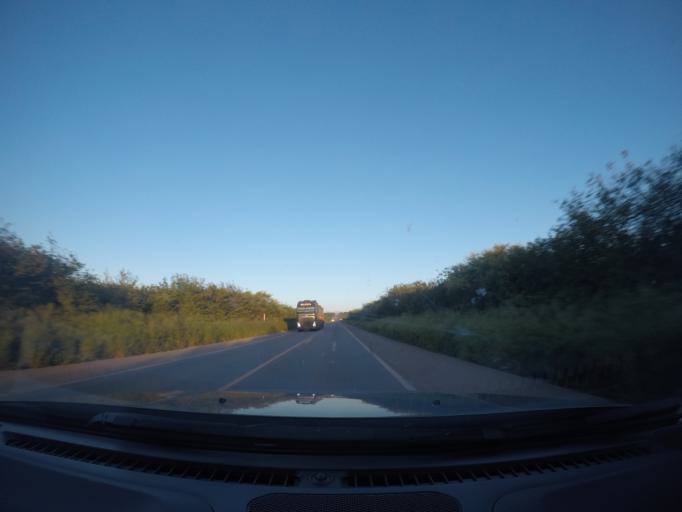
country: BR
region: Bahia
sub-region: Seabra
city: Seabra
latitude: -12.3931
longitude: -41.9227
